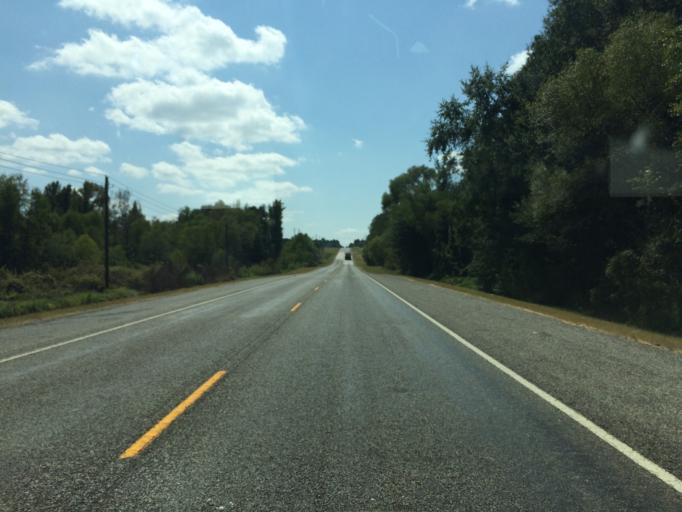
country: US
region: Texas
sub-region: Wood County
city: Hawkins
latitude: 32.7057
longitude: -95.2072
